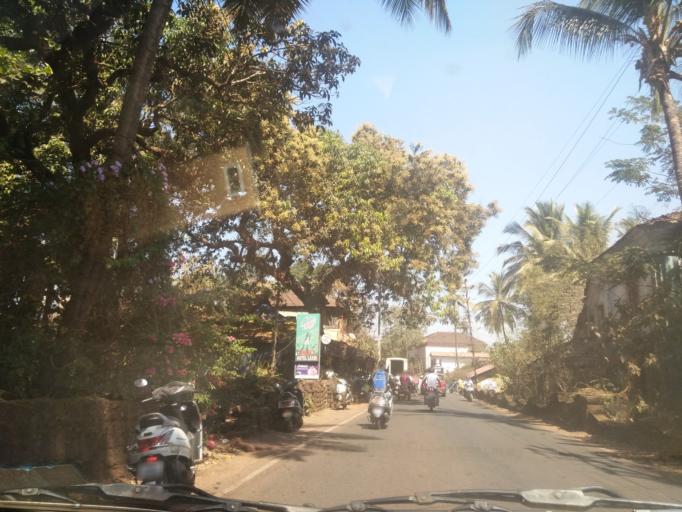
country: IN
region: Goa
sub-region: North Goa
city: Mapuca
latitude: 15.5993
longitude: 73.8157
